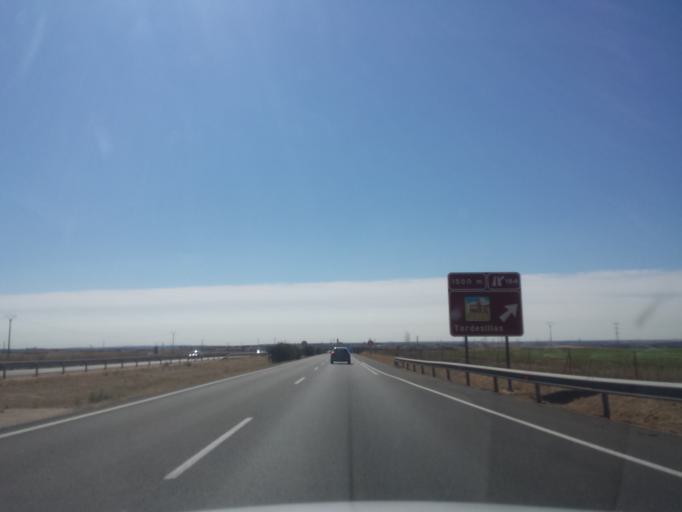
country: ES
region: Castille and Leon
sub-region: Provincia de Valladolid
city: Tordesillas
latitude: 41.5221
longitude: -5.0385
